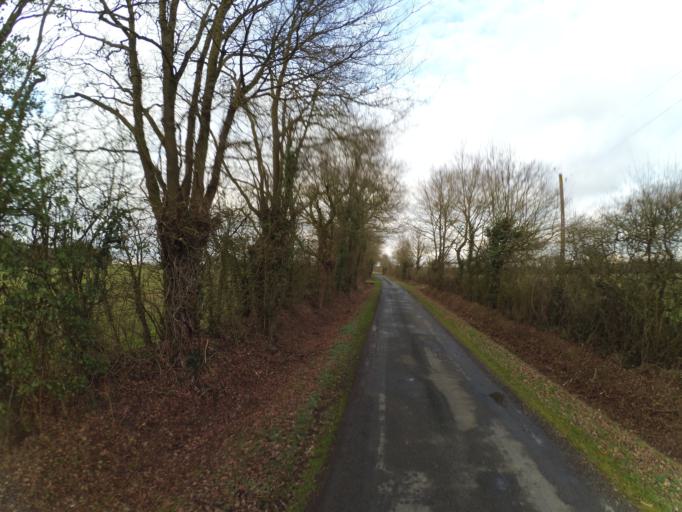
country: FR
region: Pays de la Loire
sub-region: Departement de la Loire-Atlantique
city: Saint-Hilaire-de-Clisson
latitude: 47.0411
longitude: -1.2919
